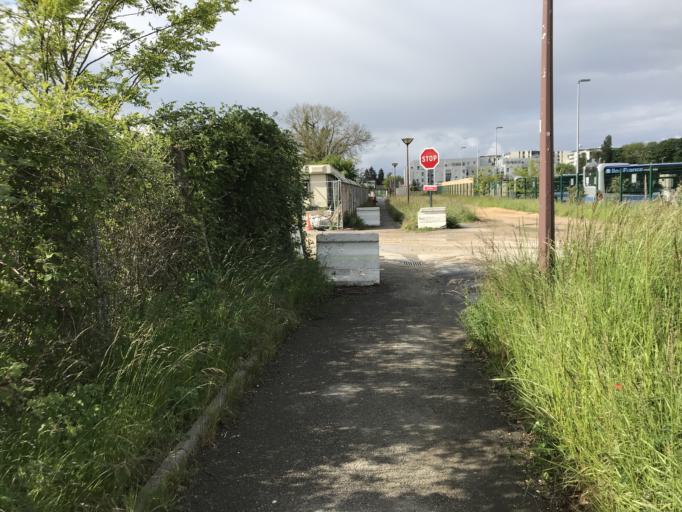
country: FR
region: Ile-de-France
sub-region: Departement des Yvelines
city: Velizy-Villacoublay
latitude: 48.7784
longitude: 2.1914
